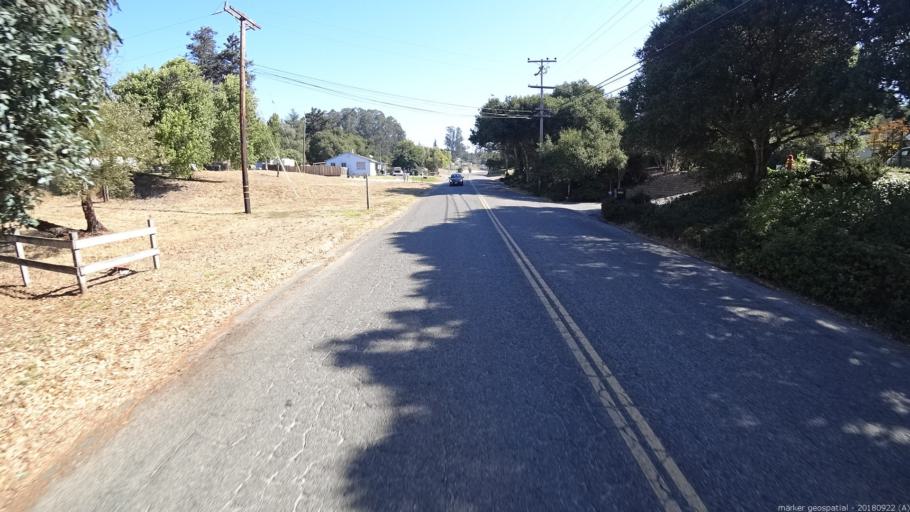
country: US
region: California
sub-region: Monterey County
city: Prunedale
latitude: 36.8083
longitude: -121.6618
